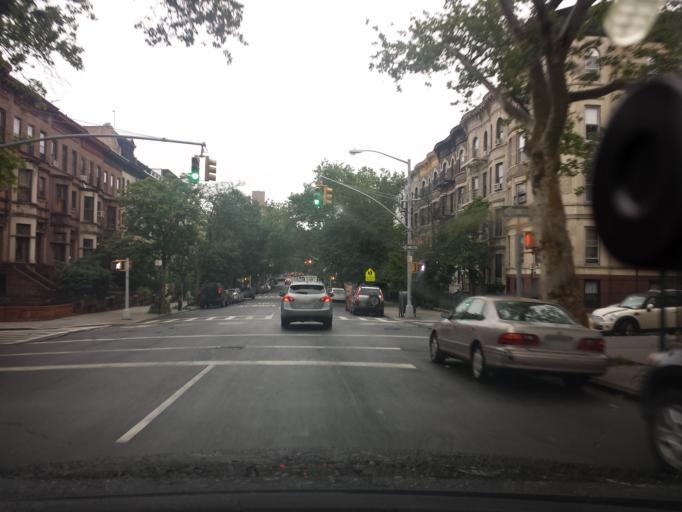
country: US
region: New York
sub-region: Kings County
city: Brooklyn
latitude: 40.6698
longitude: -73.9758
